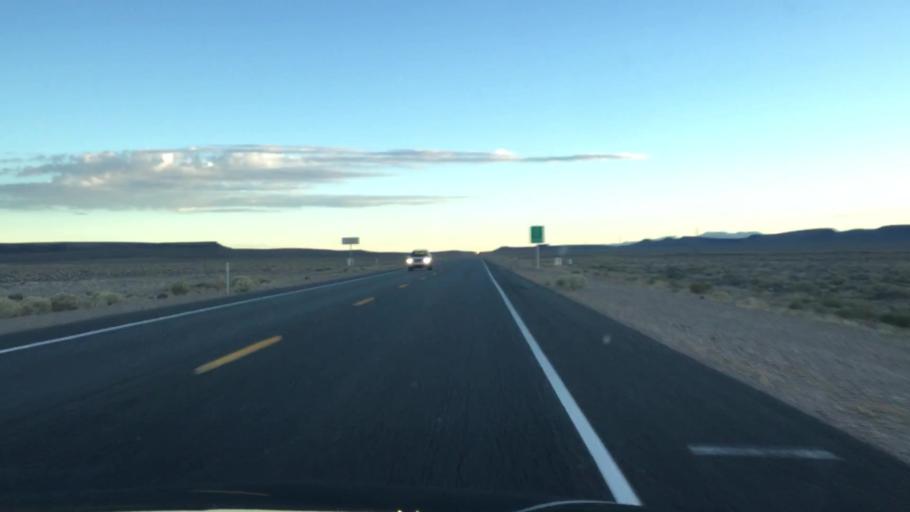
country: US
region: Nevada
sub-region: Esmeralda County
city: Goldfield
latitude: 37.4441
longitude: -117.1660
